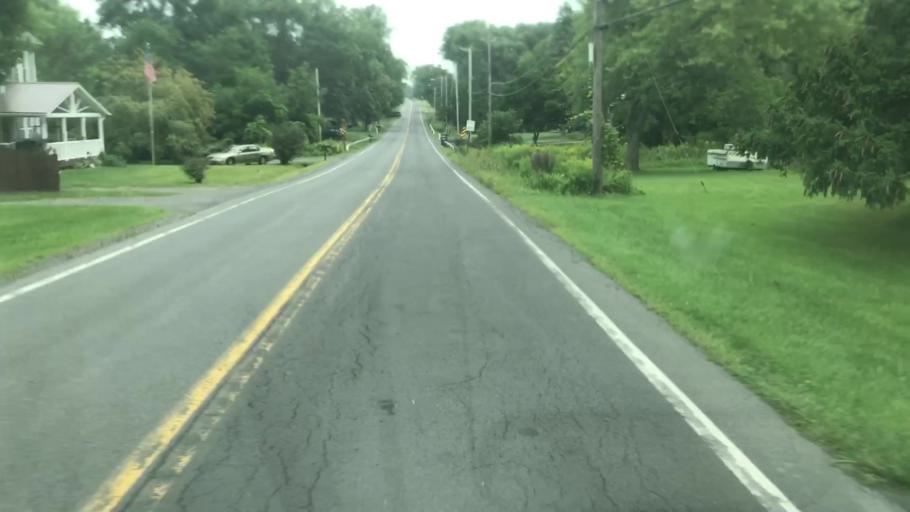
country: US
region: New York
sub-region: Cayuga County
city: Melrose Park
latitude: 42.9478
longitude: -76.5271
